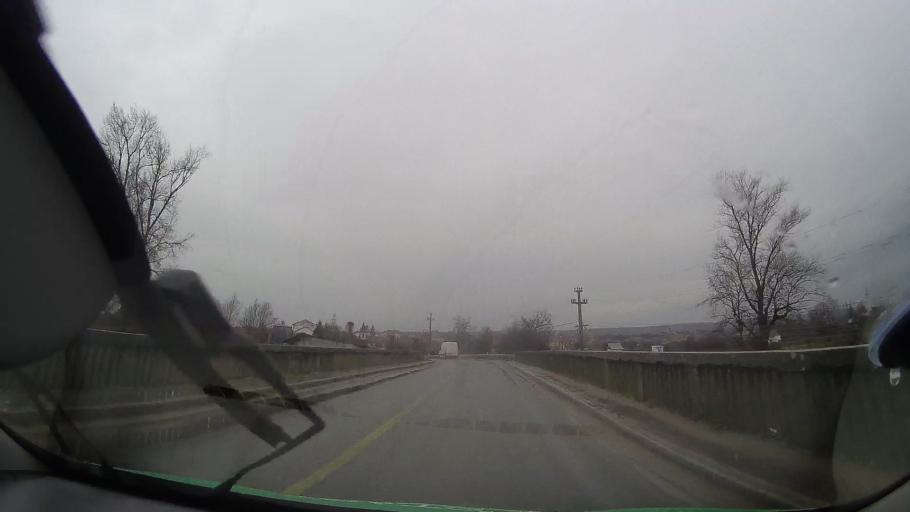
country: RO
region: Bihor
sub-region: Comuna Tinca
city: Tinca
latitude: 46.7683
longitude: 21.9329
